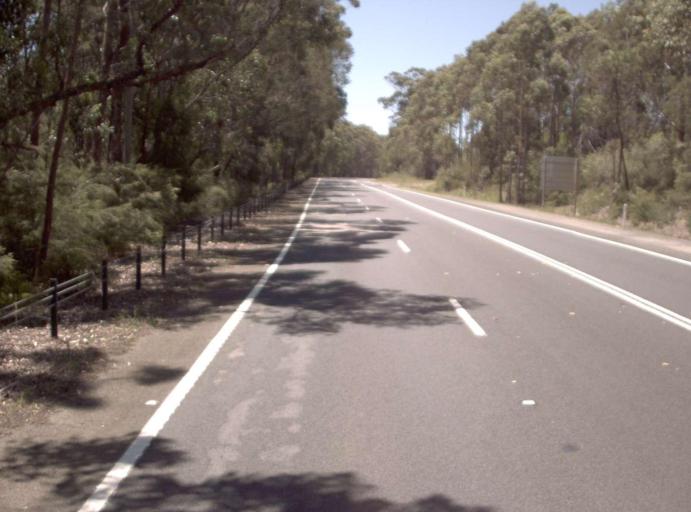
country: AU
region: Victoria
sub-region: East Gippsland
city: Lakes Entrance
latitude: -37.7320
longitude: 148.1111
